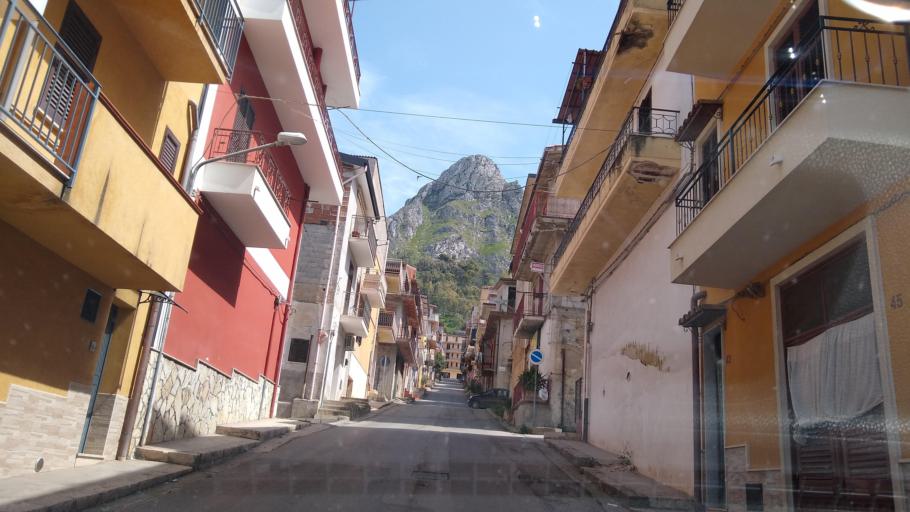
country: IT
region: Sicily
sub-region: Palermo
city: San Giuseppe Jato
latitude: 37.9722
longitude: 13.1808
